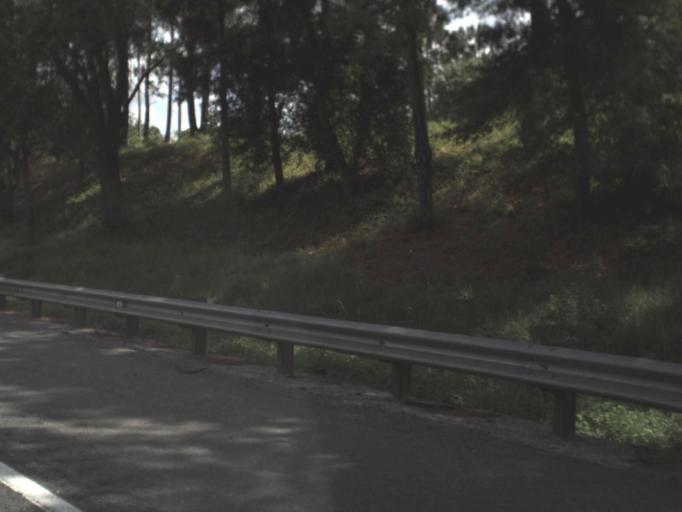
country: US
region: Florida
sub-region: Suwannee County
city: Wellborn
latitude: 30.2605
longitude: -82.7507
